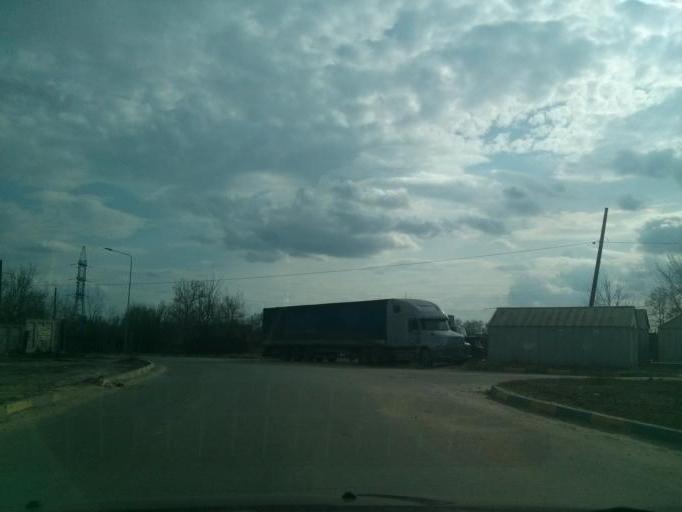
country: RU
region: Nizjnij Novgorod
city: Nizhniy Novgorod
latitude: 56.2610
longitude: 44.0091
